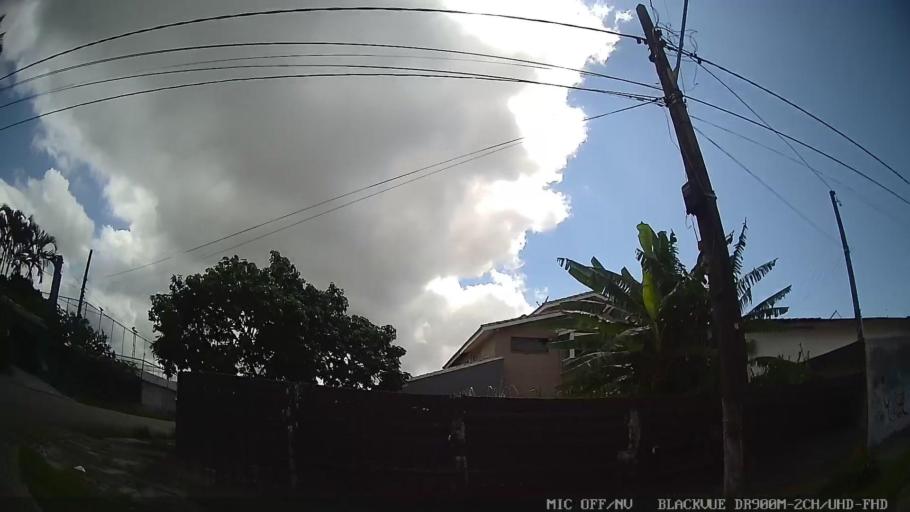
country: BR
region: Sao Paulo
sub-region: Peruibe
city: Peruibe
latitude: -24.3123
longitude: -47.0080
